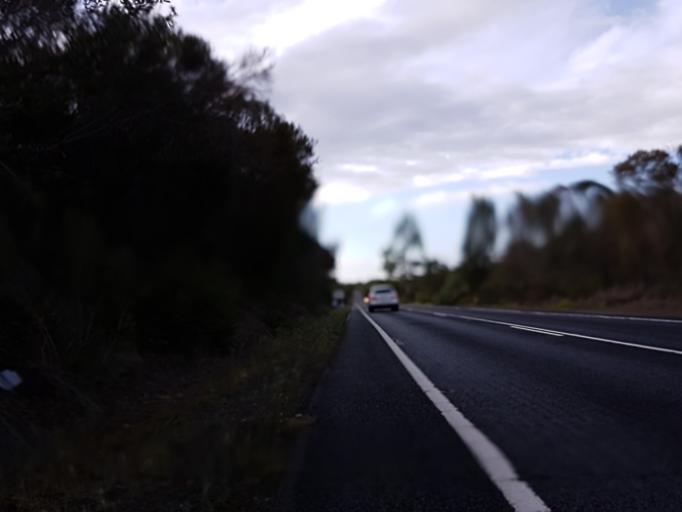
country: AU
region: New South Wales
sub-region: Warringah
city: Allambie Heights
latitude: -33.7677
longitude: 151.2343
